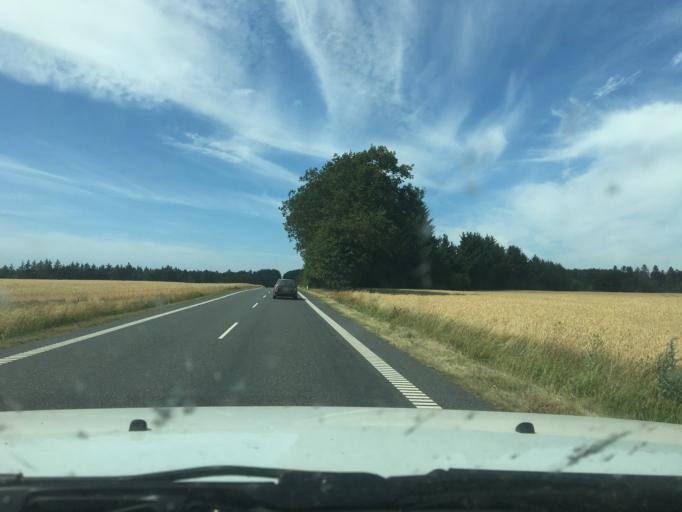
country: DK
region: Central Jutland
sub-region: Viborg Kommune
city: Viborg
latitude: 56.6006
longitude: 9.3598
